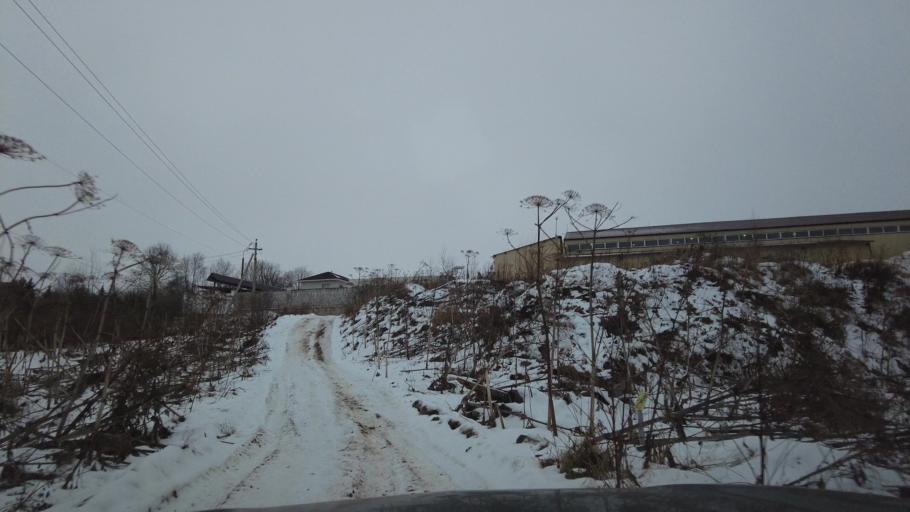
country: RU
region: Moskovskaya
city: Novopodrezkovo
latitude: 55.9903
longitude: 37.3932
